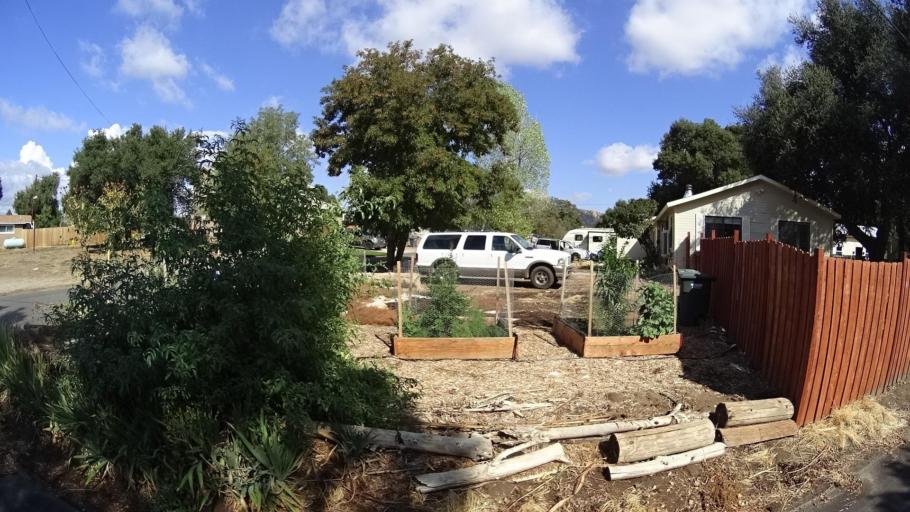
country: US
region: California
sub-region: San Diego County
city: Campo
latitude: 32.6802
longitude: -116.5089
